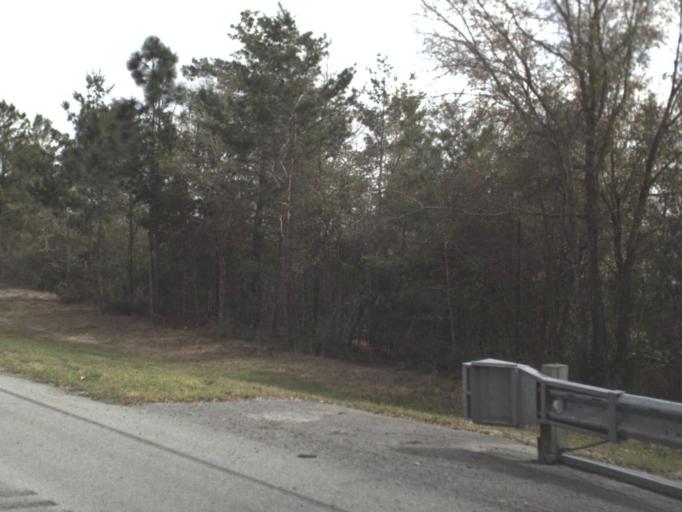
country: US
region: Florida
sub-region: Walton County
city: DeFuniak Springs
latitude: 30.7281
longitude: -86.2131
